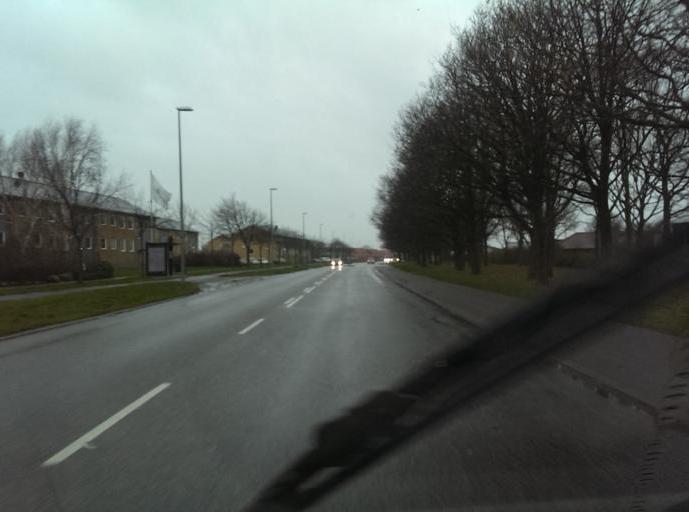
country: DK
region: South Denmark
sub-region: Esbjerg Kommune
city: Esbjerg
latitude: 55.4868
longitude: 8.4819
